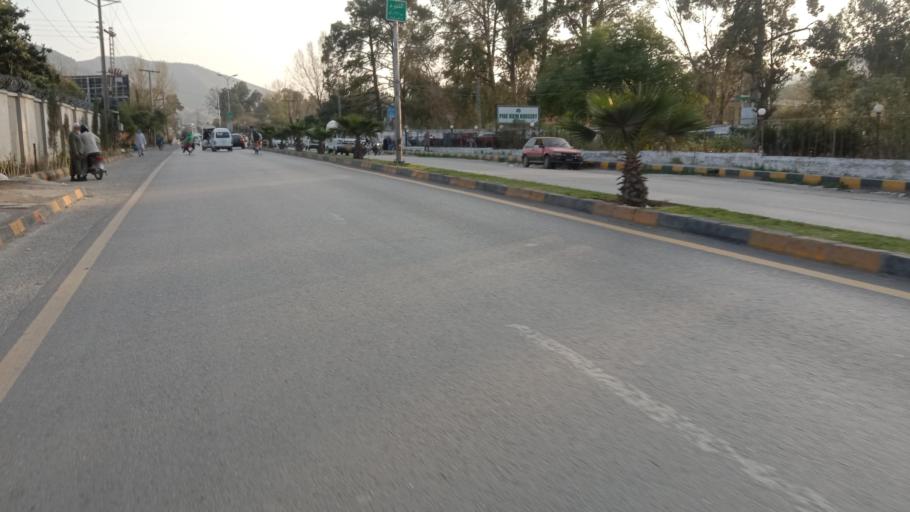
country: PK
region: Khyber Pakhtunkhwa
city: Abbottabad
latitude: 34.1621
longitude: 73.2220
